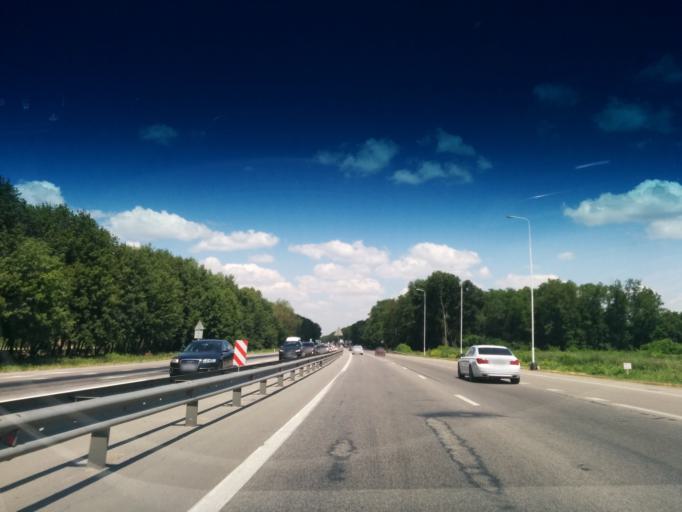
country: RU
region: Rostov
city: Aksay
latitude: 47.3020
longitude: 39.8630
